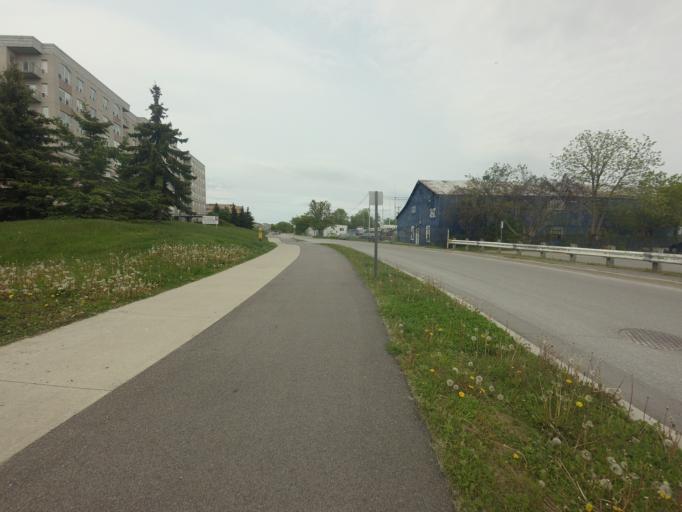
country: CA
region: Ontario
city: Kingston
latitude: 44.2359
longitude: -76.4812
